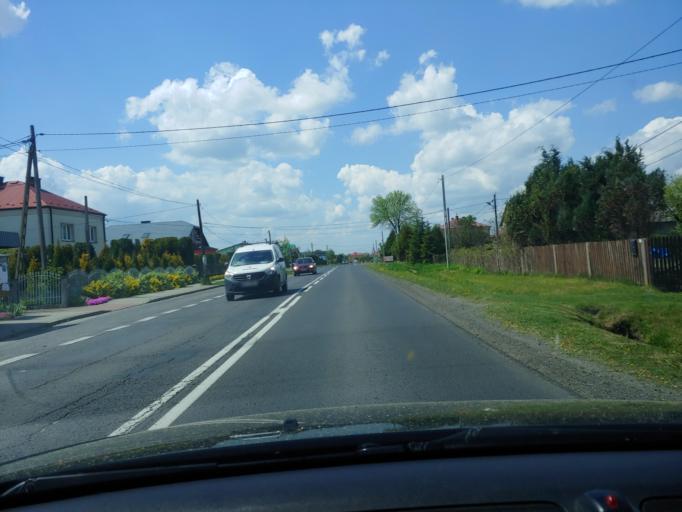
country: PL
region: Subcarpathian Voivodeship
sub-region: Powiat mielecki
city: Wadowice Gorne
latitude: 50.2593
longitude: 21.3414
